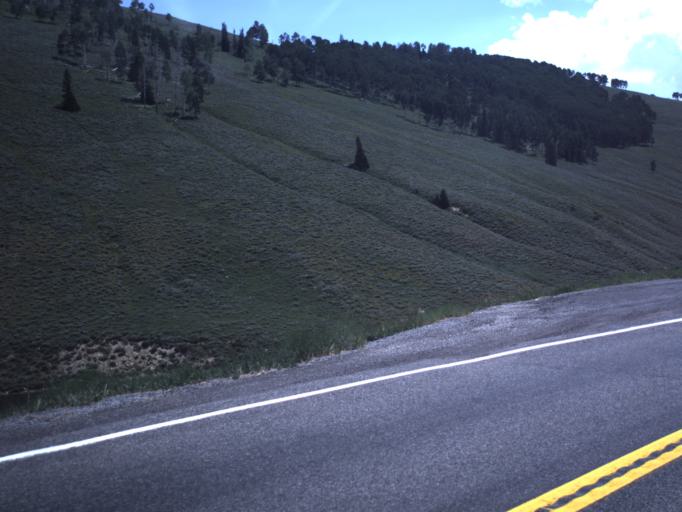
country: US
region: Utah
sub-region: Sanpete County
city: Fairview
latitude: 39.6455
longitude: -111.2385
